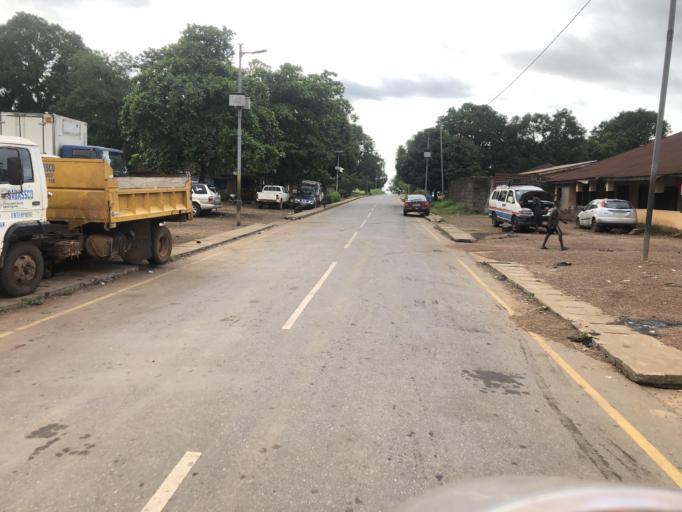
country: SL
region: Northern Province
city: Port Loko
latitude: 8.7723
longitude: -12.7918
